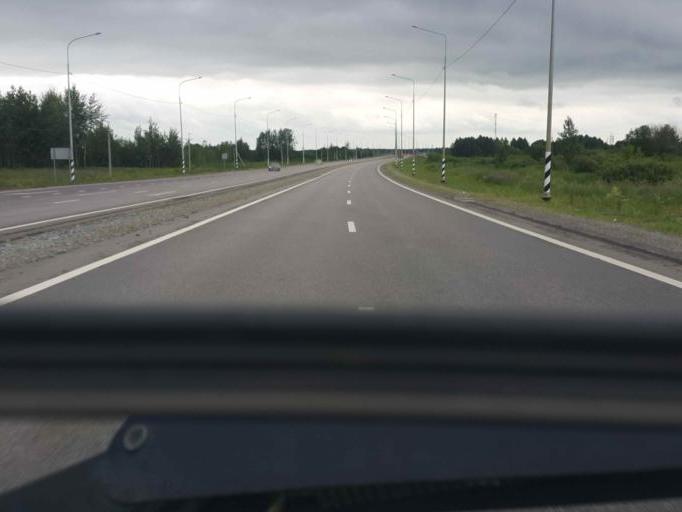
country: RU
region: Tambov
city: Zavoronezhskoye
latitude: 52.8637
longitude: 40.7642
